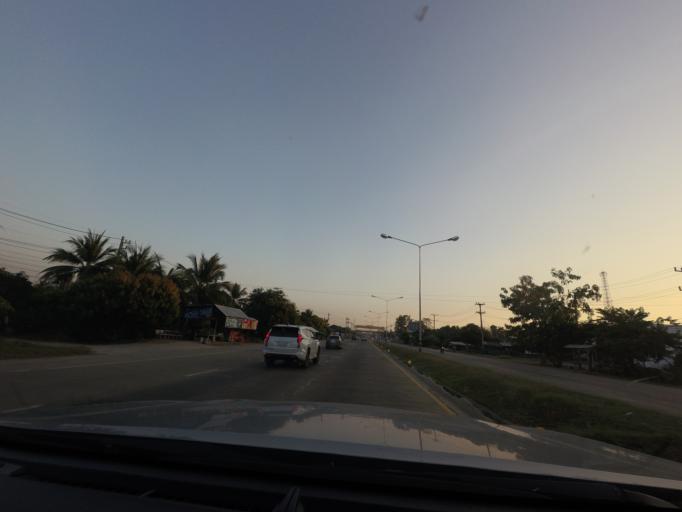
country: TH
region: Sukhothai
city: Sukhothai
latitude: 17.0726
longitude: 99.8395
